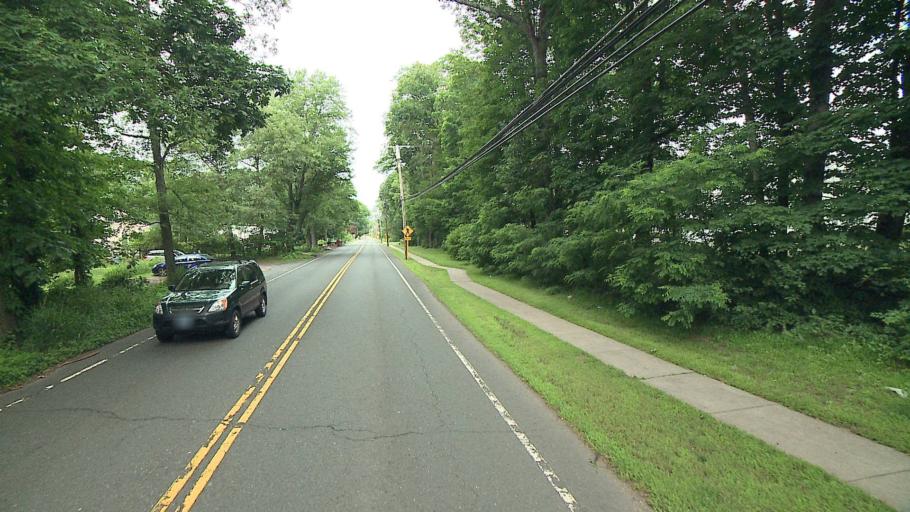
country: US
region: Connecticut
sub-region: Hartford County
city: Canton Valley
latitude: 41.8242
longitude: -72.9030
